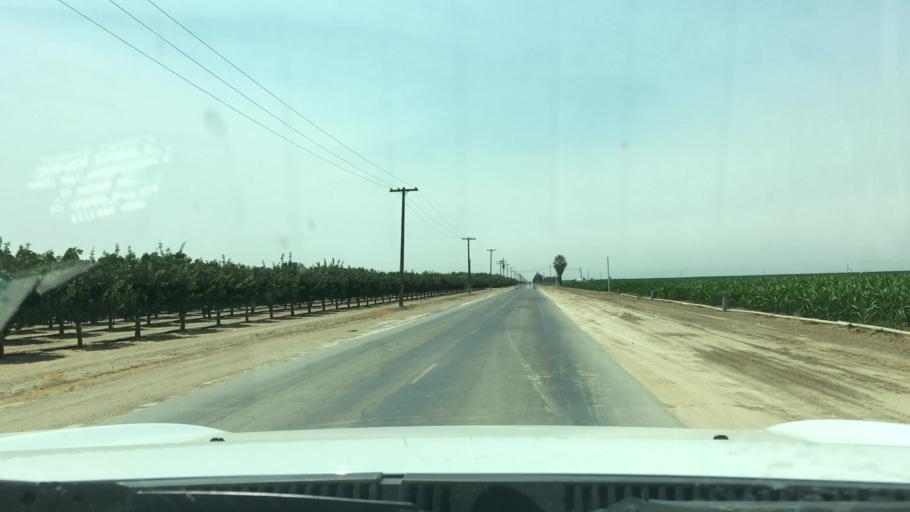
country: US
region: California
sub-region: Kern County
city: Wasco
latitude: 35.6771
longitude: -119.4374
